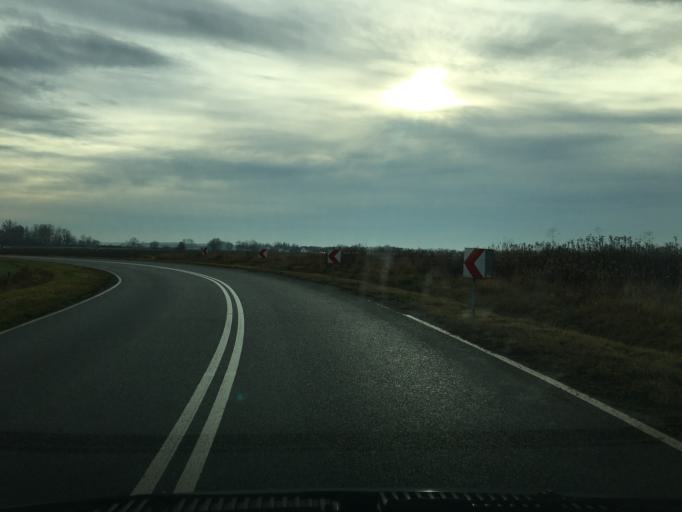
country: PL
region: Lower Silesian Voivodeship
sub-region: Powiat wroclawski
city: Dlugoleka
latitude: 51.1748
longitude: 17.2207
